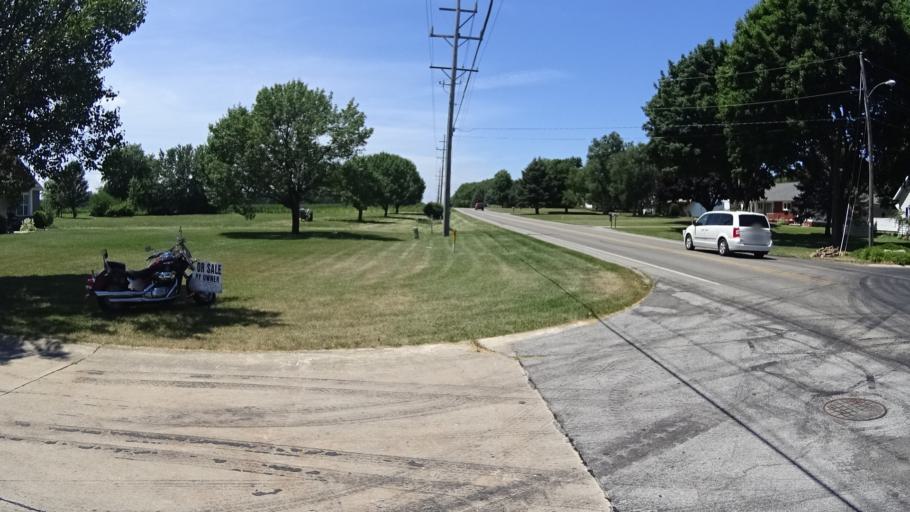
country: US
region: Ohio
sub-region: Erie County
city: Sandusky
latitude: 41.3957
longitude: -82.6572
